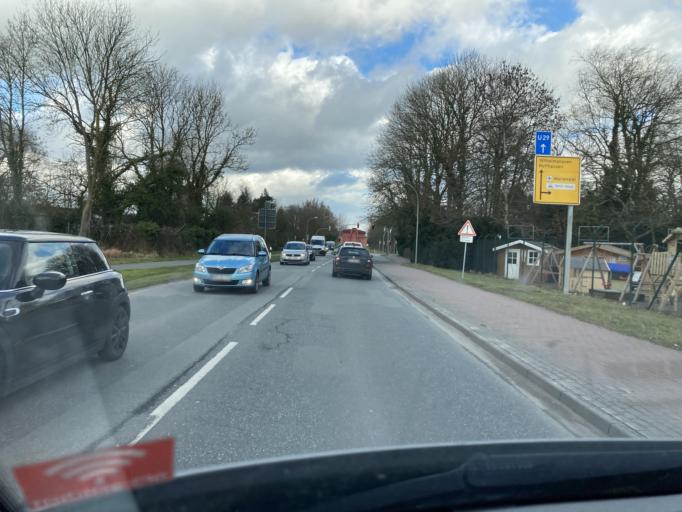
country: DE
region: Lower Saxony
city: Sande
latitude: 53.4962
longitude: 8.0247
